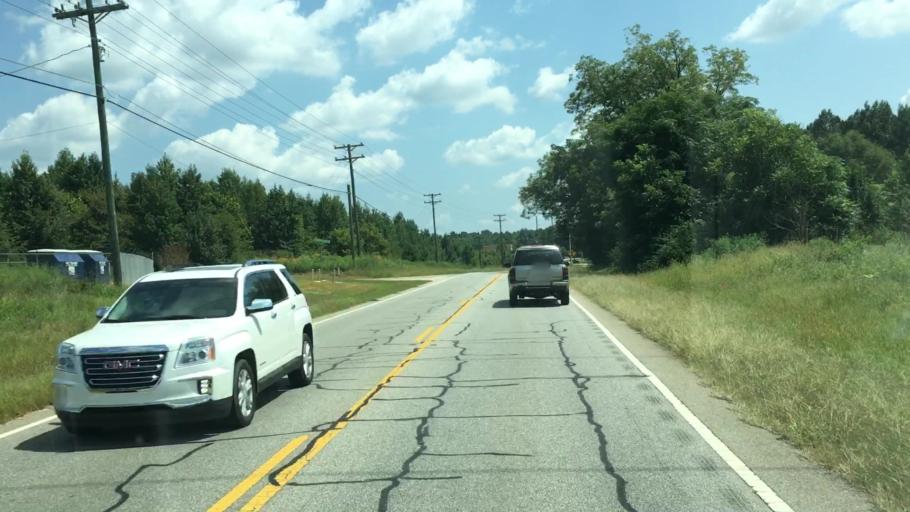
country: US
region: Georgia
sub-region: Oconee County
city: Bogart
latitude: 33.9021
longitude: -83.5772
